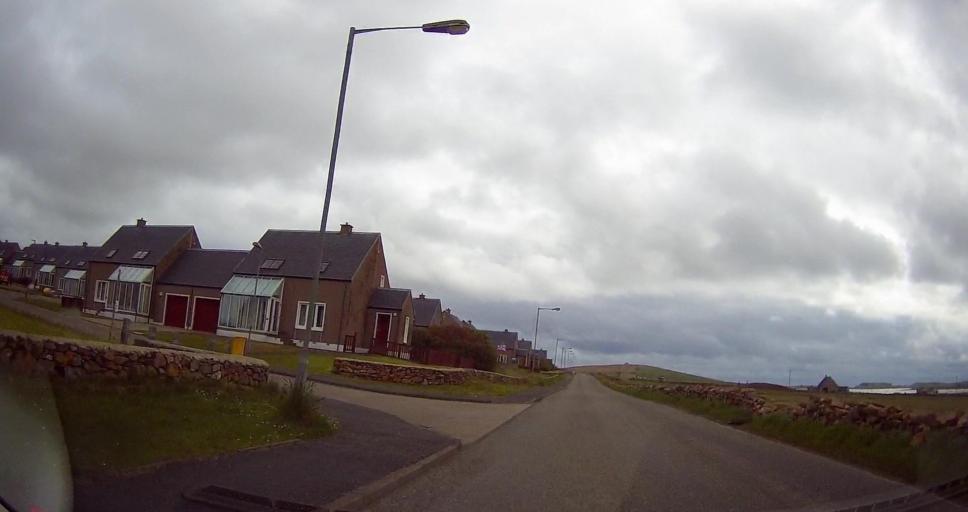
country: GB
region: Scotland
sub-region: Shetland Islands
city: Shetland
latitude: 60.7624
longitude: -0.8647
